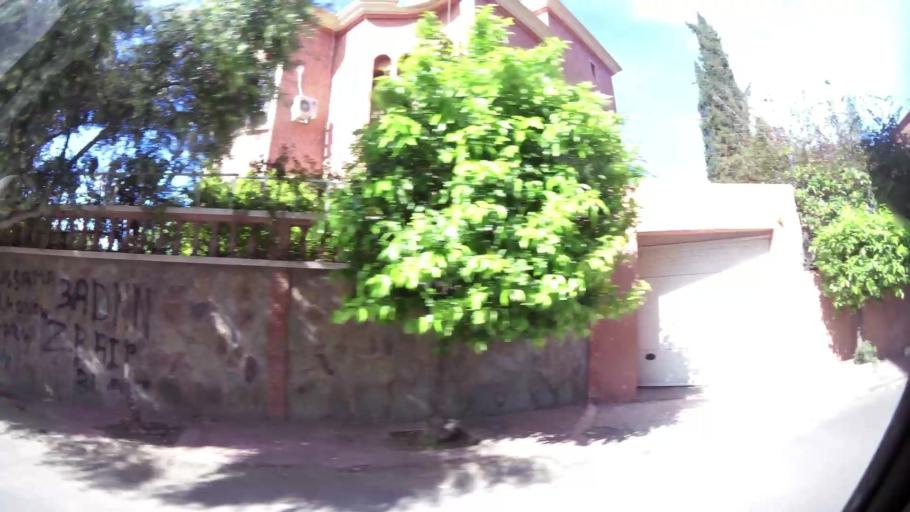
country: MA
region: Marrakech-Tensift-Al Haouz
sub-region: Marrakech
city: Marrakesh
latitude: 31.6467
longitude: -8.0092
